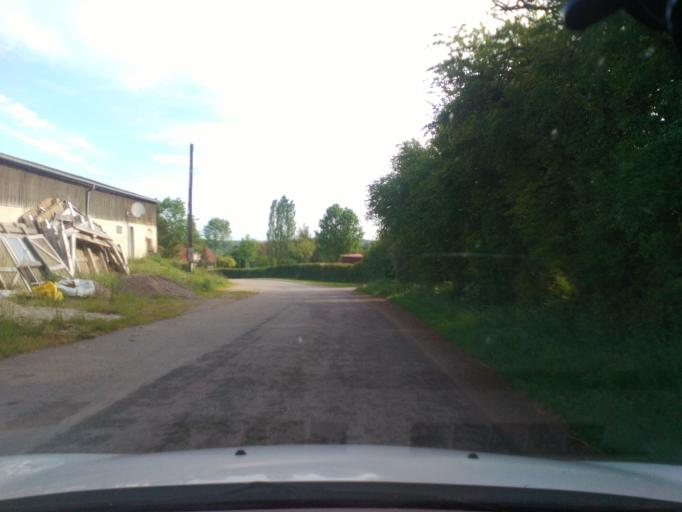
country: FR
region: Lorraine
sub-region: Departement des Vosges
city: Mirecourt
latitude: 48.3456
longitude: 6.1620
